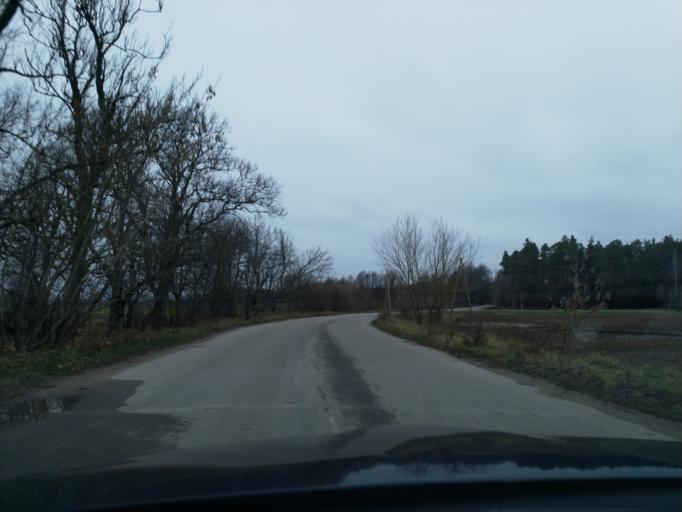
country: LV
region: Ventspils Rajons
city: Piltene
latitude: 57.1186
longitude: 21.8114
